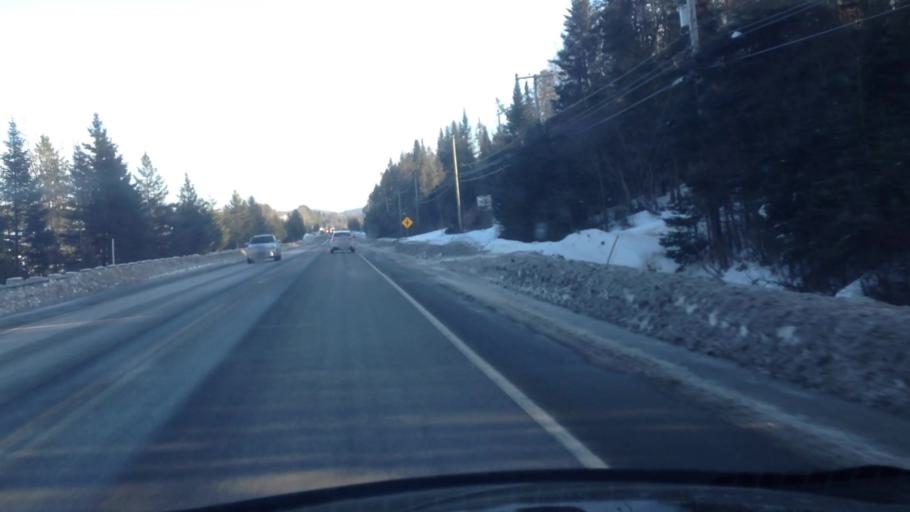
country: CA
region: Quebec
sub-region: Laurentides
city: Saint-Sauveur
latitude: 45.8976
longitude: -74.2089
